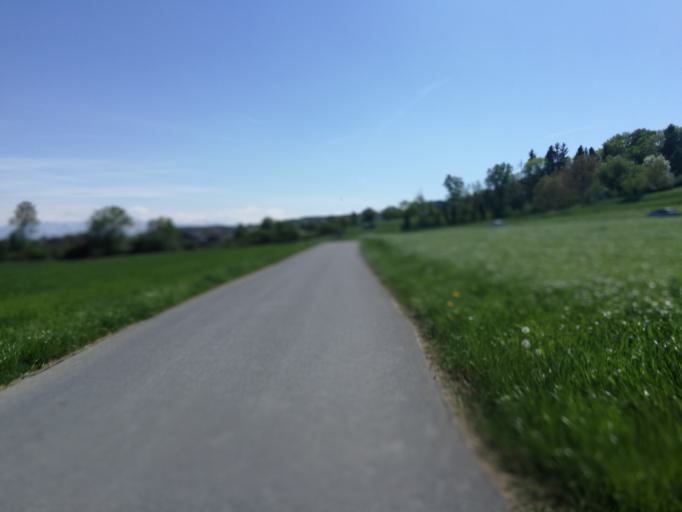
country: CH
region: Zurich
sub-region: Bezirk Uster
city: Aesch
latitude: 47.3468
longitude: 8.6648
